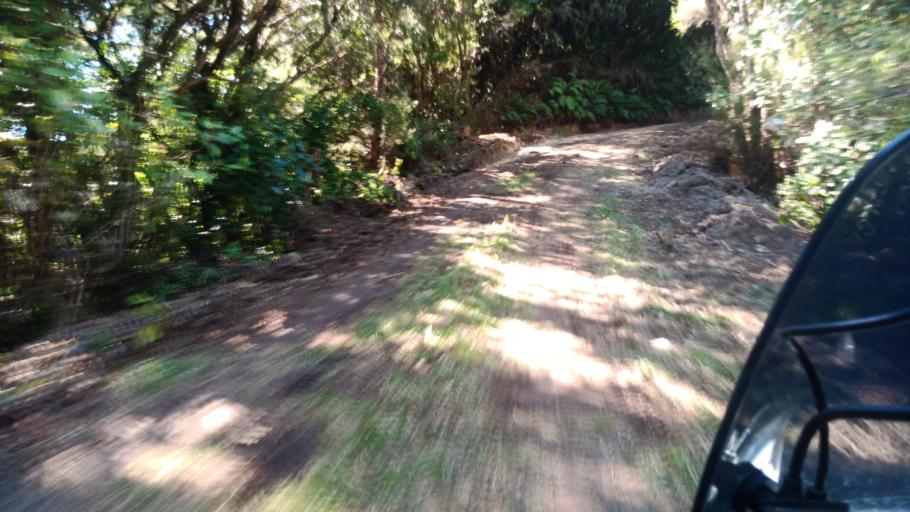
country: NZ
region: Hawke's Bay
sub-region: Wairoa District
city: Wairoa
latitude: -38.9985
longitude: 177.0676
